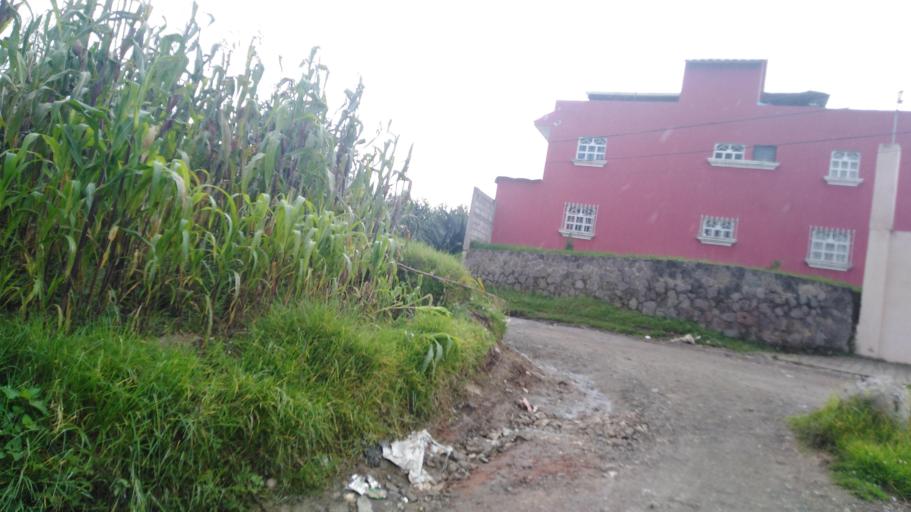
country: GT
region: Quetzaltenango
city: Olintepeque
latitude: 14.8634
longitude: -91.5009
